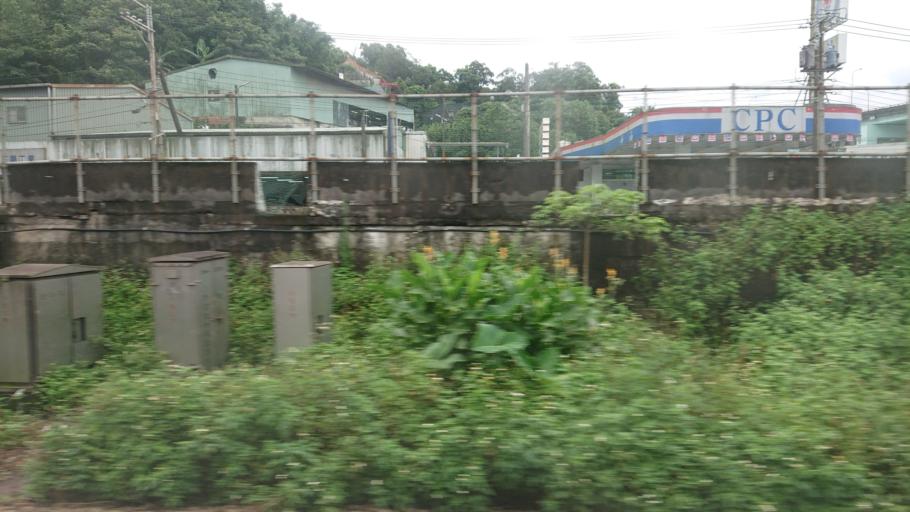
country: TW
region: Taiwan
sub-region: Keelung
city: Keelung
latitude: 25.1063
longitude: 121.7263
